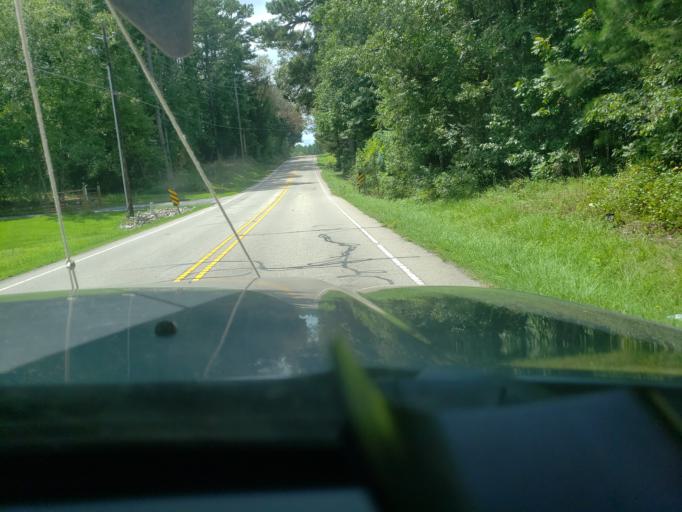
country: US
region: North Carolina
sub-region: Wake County
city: Rolesville
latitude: 35.8779
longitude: -78.4588
